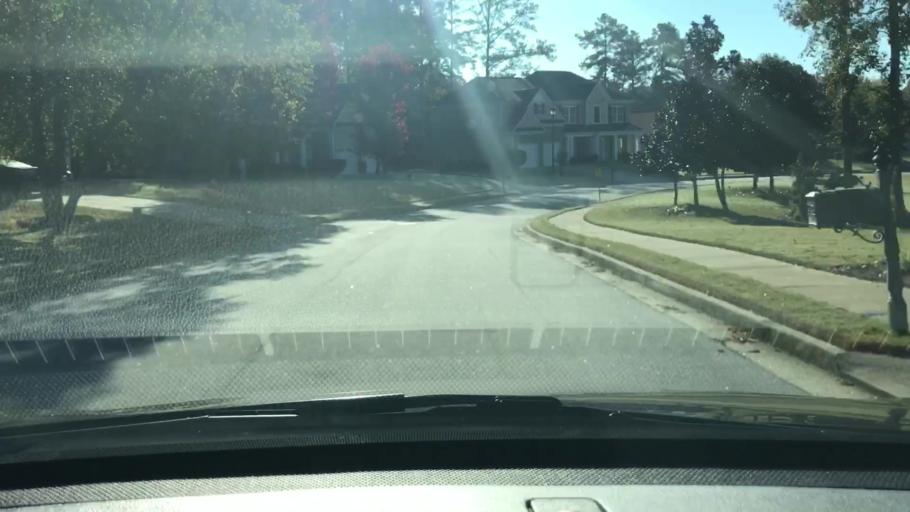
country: US
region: Georgia
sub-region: Douglas County
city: Douglasville
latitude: 33.7393
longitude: -84.7577
